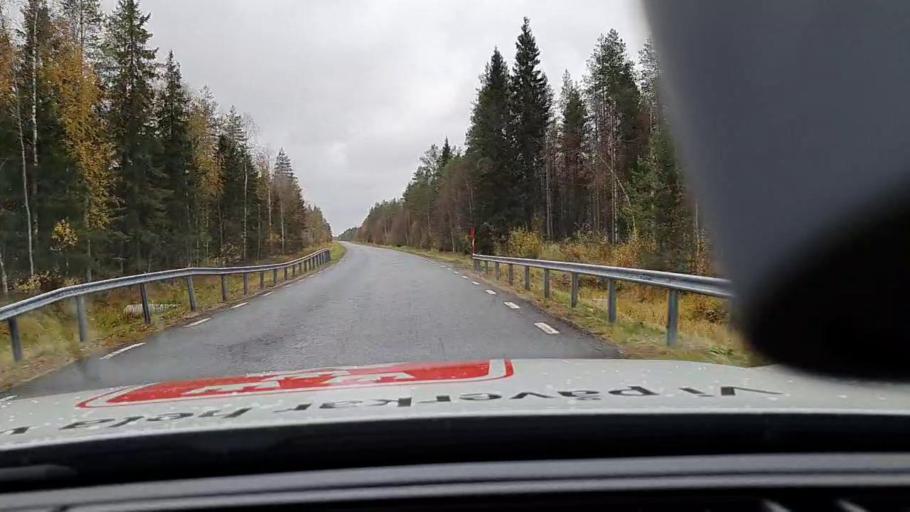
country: SE
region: Norrbotten
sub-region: Haparanda Kommun
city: Haparanda
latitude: 65.9044
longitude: 23.8333
